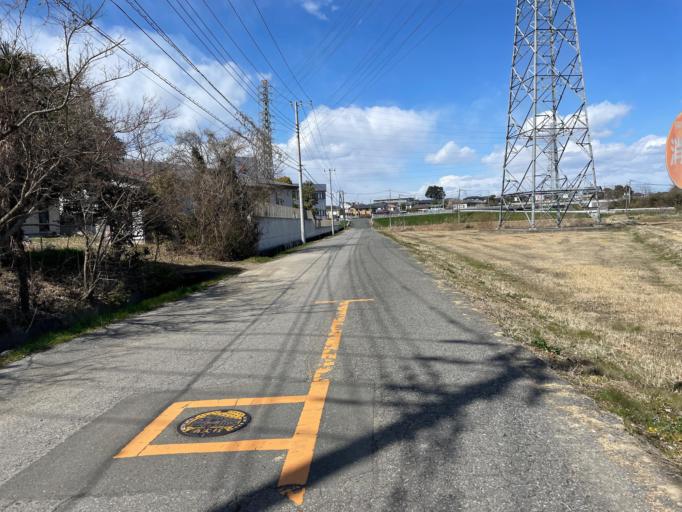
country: JP
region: Saitama
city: Sakado
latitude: 35.9924
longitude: 139.4056
